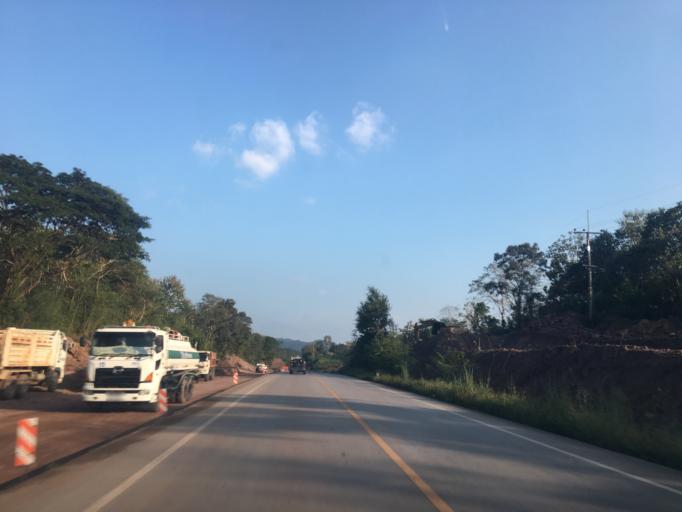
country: TH
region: Lampang
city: Ngao
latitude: 18.7120
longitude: 99.9850
